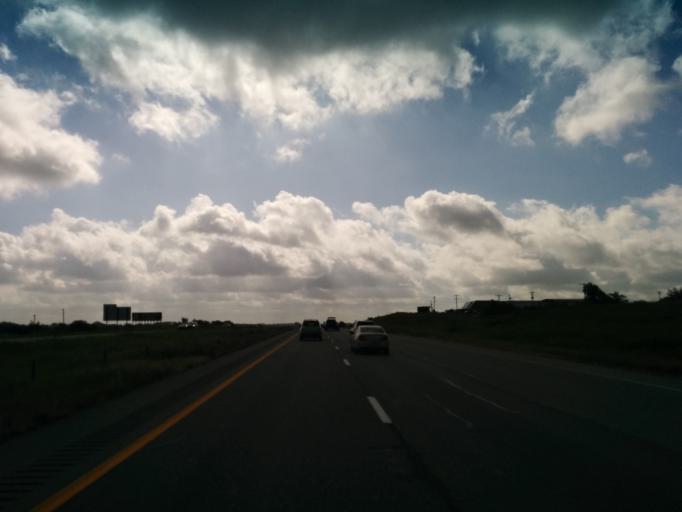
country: US
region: Texas
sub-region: Caldwell County
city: Luling
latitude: 29.6508
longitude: -97.6556
